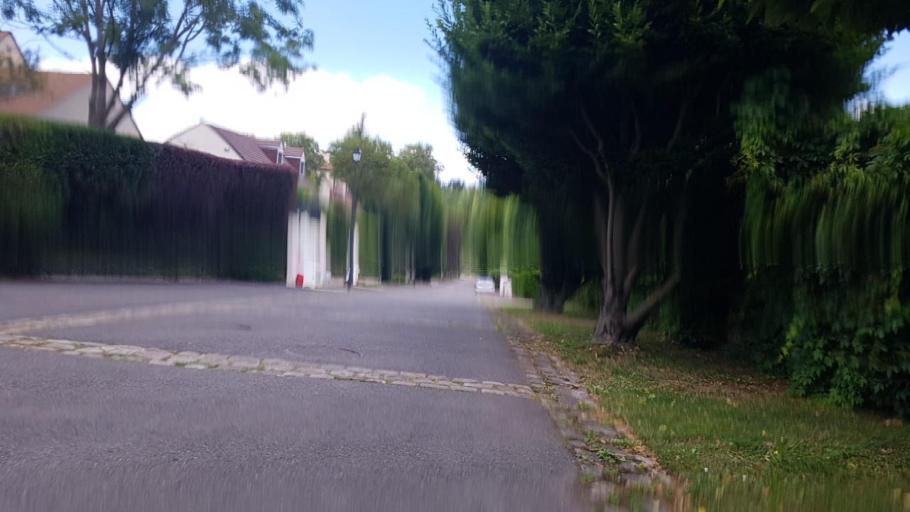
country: FR
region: Ile-de-France
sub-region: Departement de Seine-et-Marne
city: Claye-Souilly
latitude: 48.9671
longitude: 2.6732
